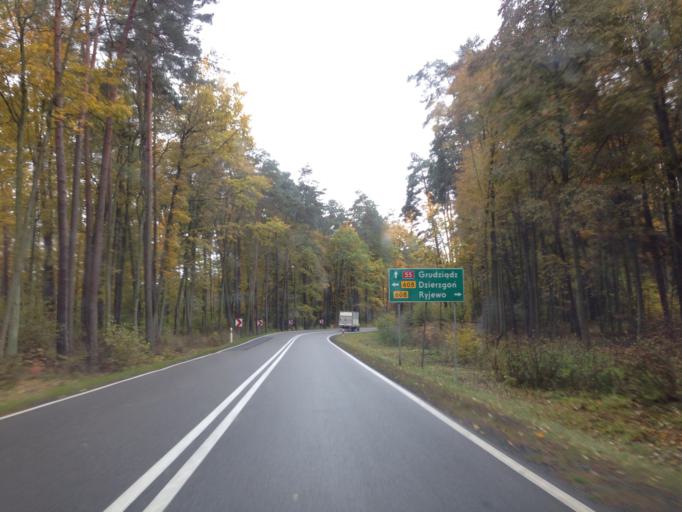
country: PL
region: Pomeranian Voivodeship
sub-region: Powiat kwidzynski
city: Ryjewo
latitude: 53.8378
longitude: 18.9969
